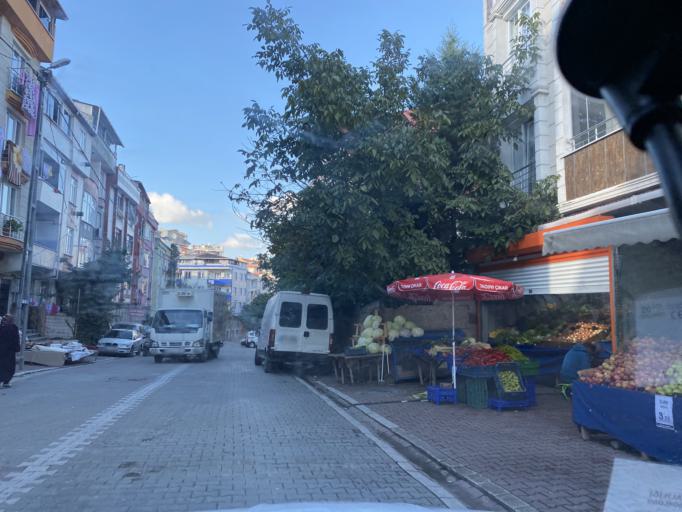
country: TR
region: Istanbul
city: Esenyurt
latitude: 41.0362
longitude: 28.6514
